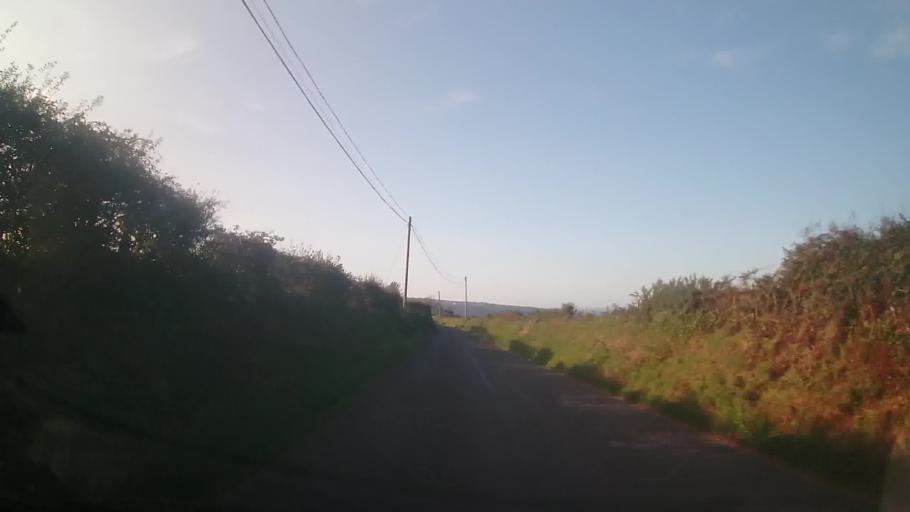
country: GB
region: Wales
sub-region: Pembrokeshire
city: Fishguard
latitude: 51.9861
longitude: -4.9582
